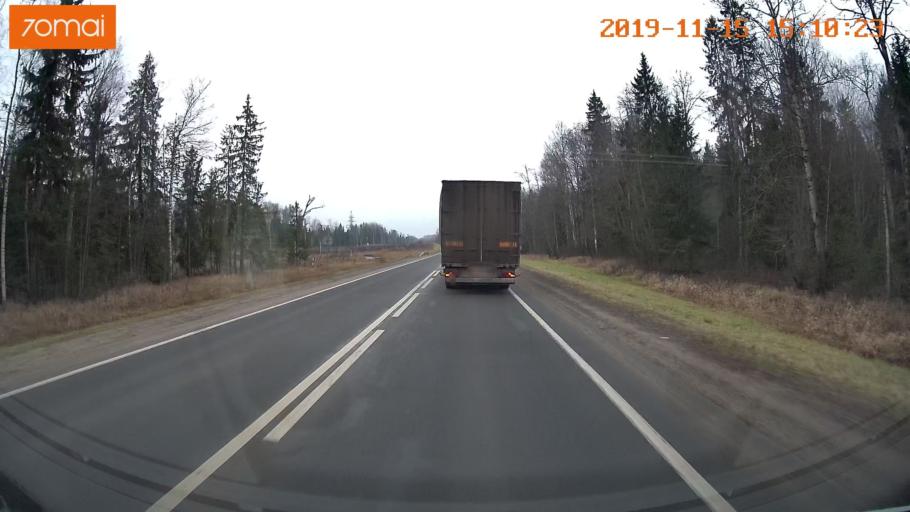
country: RU
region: Jaroslavl
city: Prechistoye
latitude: 58.3483
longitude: 40.2543
